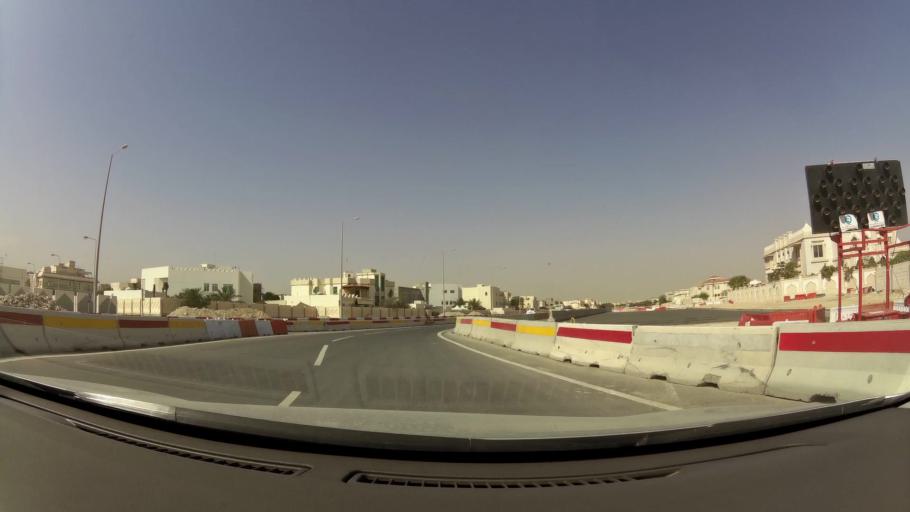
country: QA
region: Baladiyat ad Dawhah
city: Doha
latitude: 25.3523
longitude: 51.5123
